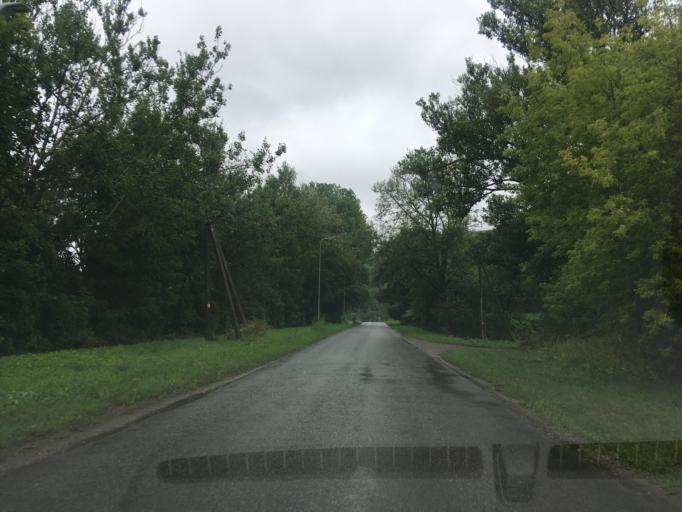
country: EE
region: Ida-Virumaa
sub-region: Kivioli linn
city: Kivioli
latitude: 59.3582
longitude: 26.9590
